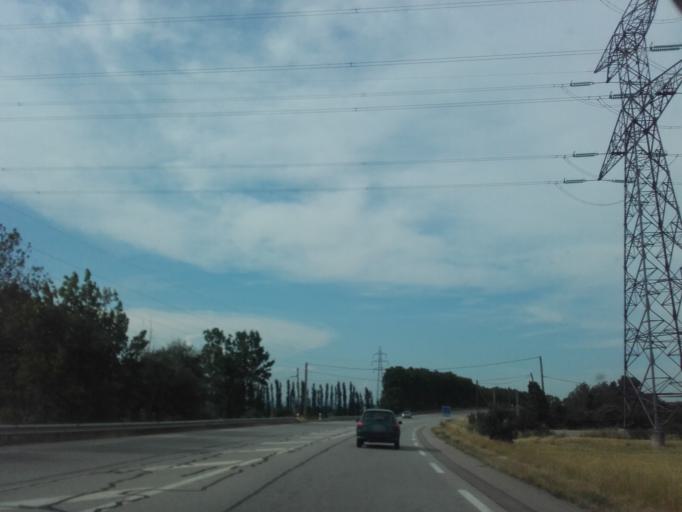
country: FR
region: Rhone-Alpes
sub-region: Departement de la Drome
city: Saulce-sur-Rhone
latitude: 44.6817
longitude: 4.7940
